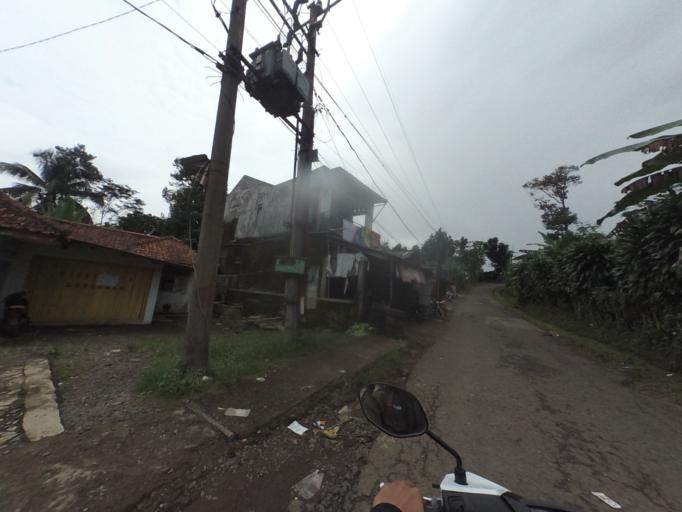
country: ID
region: West Java
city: Bogor
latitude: -6.6382
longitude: 106.7356
